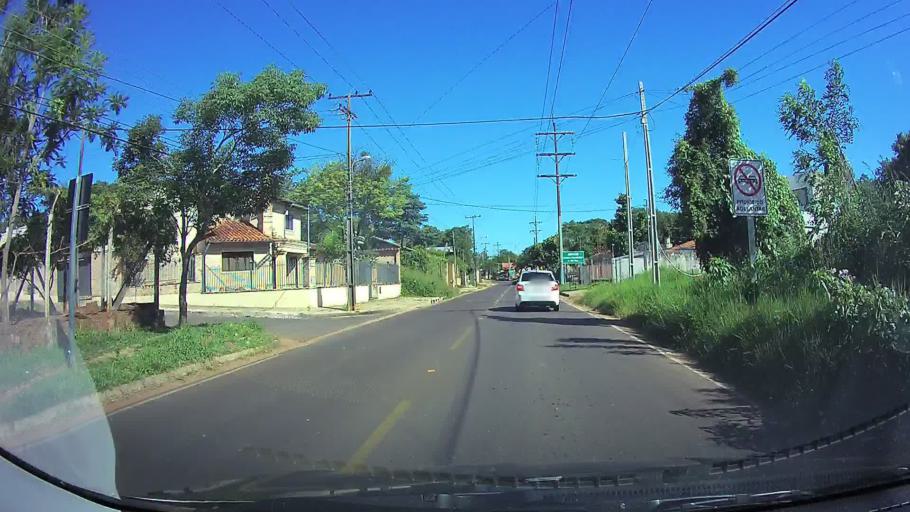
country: PY
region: Central
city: Fernando de la Mora
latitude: -25.3157
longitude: -57.5219
